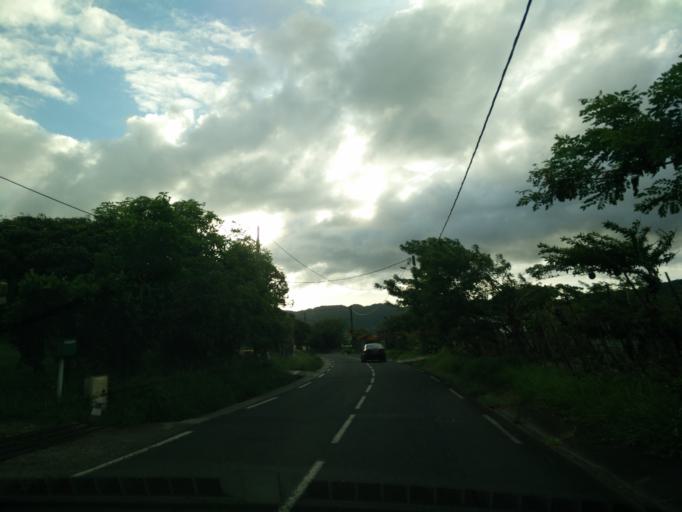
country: MQ
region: Martinique
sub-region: Martinique
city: Le Marin
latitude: 14.4639
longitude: -60.8529
